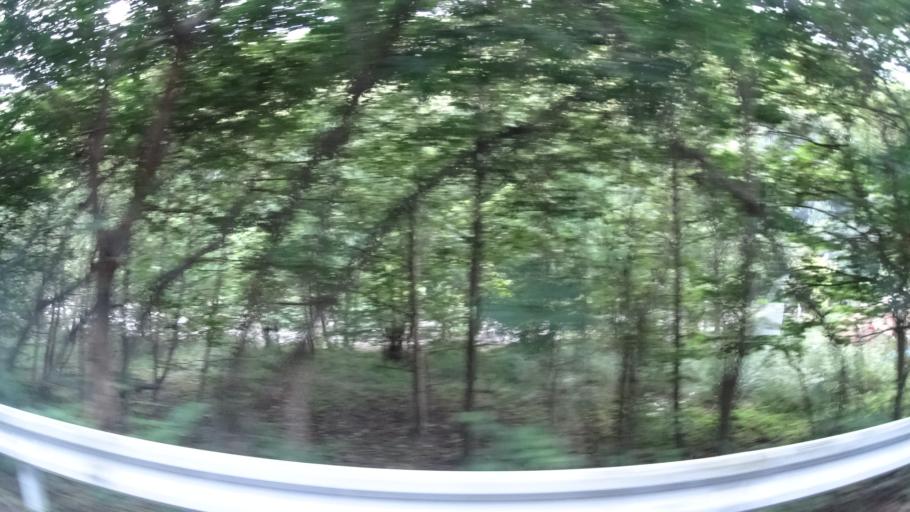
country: JP
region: Tochigi
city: Nikko
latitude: 36.6920
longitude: 139.4999
